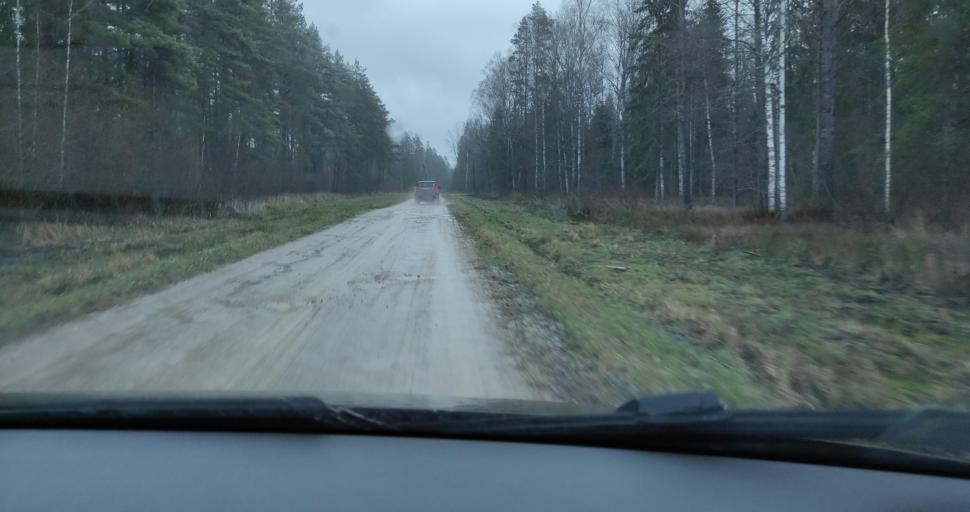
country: LV
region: Skrunda
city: Skrunda
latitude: 56.6045
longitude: 22.1242
